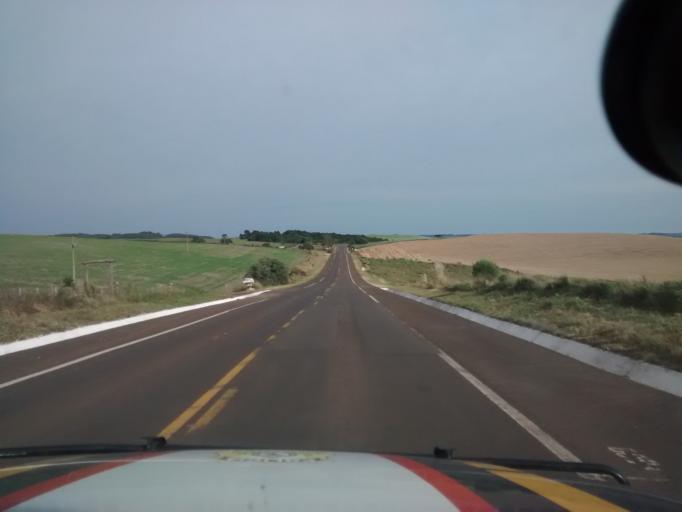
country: BR
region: Rio Grande do Sul
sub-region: Lagoa Vermelha
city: Lagoa Vermelha
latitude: -28.3259
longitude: -51.2620
